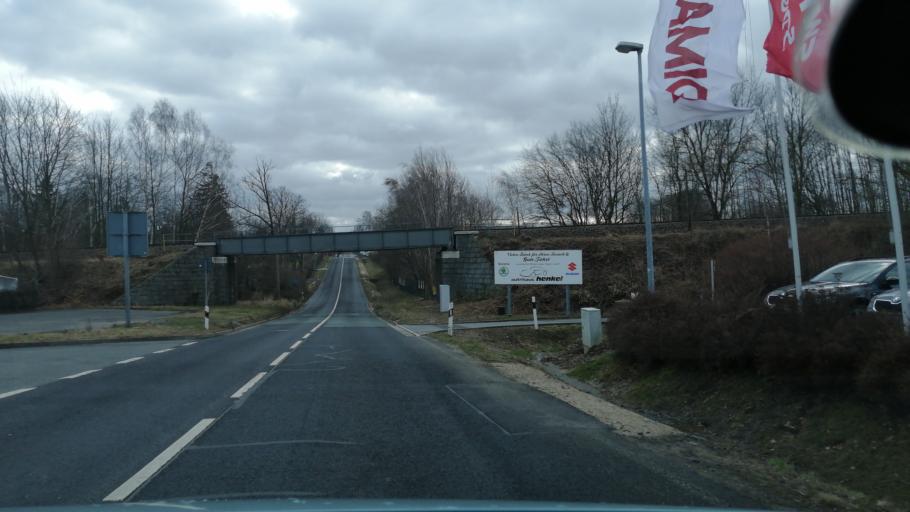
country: DE
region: Saxony
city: Lobau
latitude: 51.1038
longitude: 14.6547
